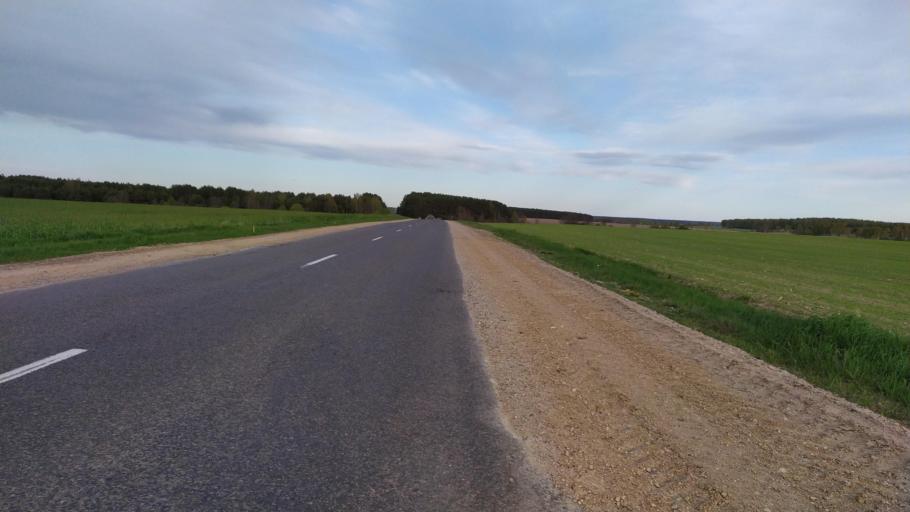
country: BY
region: Brest
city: Kamyanyets
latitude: 52.4105
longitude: 23.7250
